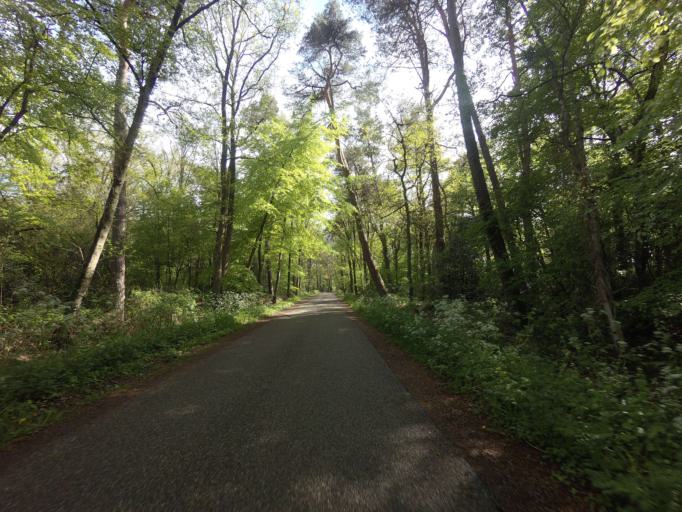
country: NL
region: Overijssel
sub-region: Gemeente Hengelo
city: Hengelo
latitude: 52.1971
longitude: 6.8068
